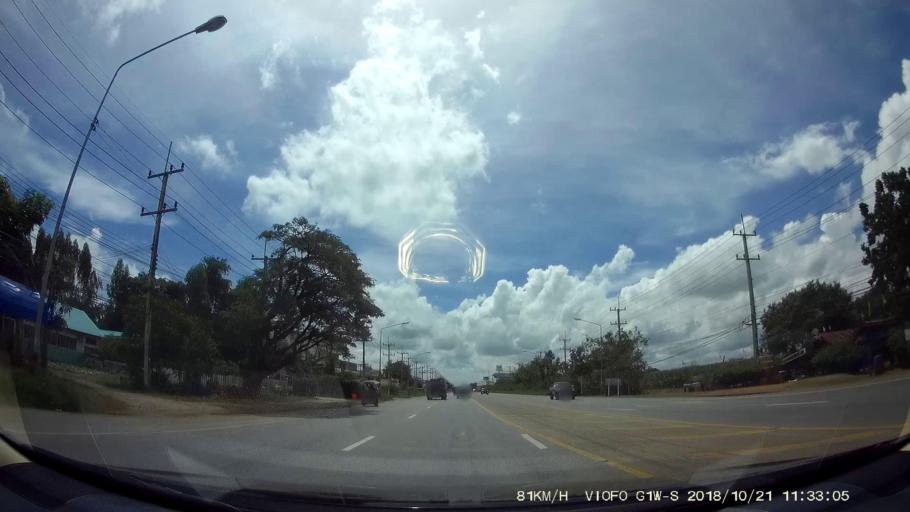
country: TH
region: Chaiyaphum
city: Chaiyaphum
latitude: 15.7500
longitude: 102.0241
